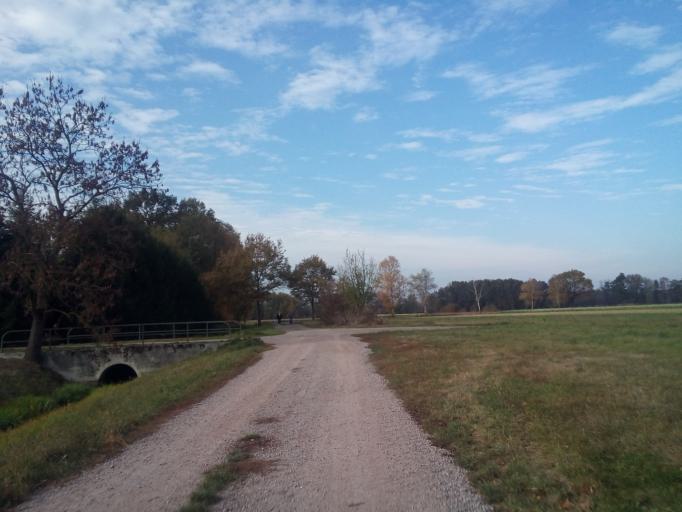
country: DE
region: Baden-Wuerttemberg
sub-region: Karlsruhe Region
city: Zell
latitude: 48.6723
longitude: 8.0439
